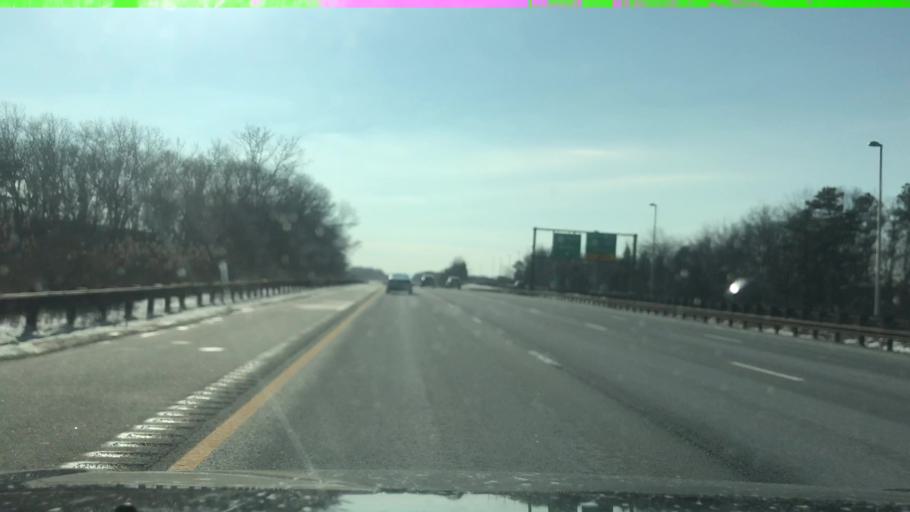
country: US
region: New Jersey
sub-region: Monmouth County
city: Shark River Hills
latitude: 40.1680
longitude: -74.1014
